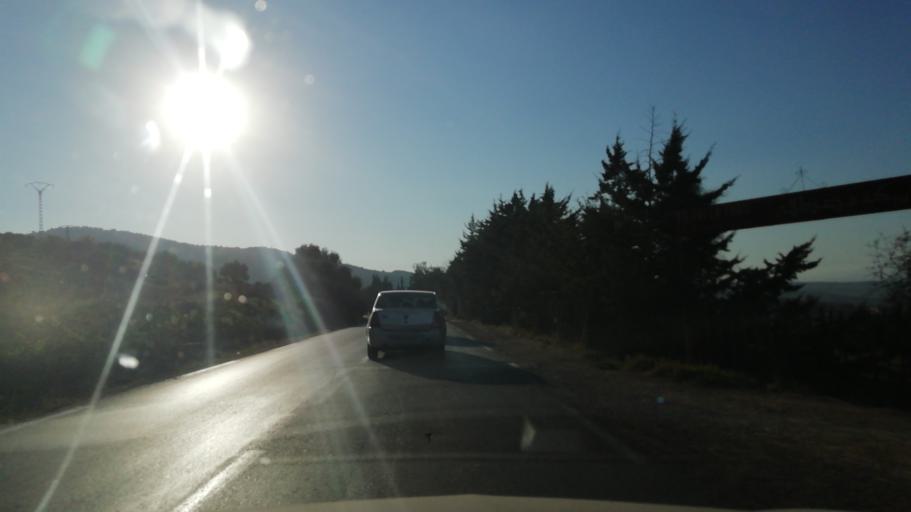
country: DZ
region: Tlemcen
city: Beni Mester
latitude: 34.8638
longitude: -1.4333
